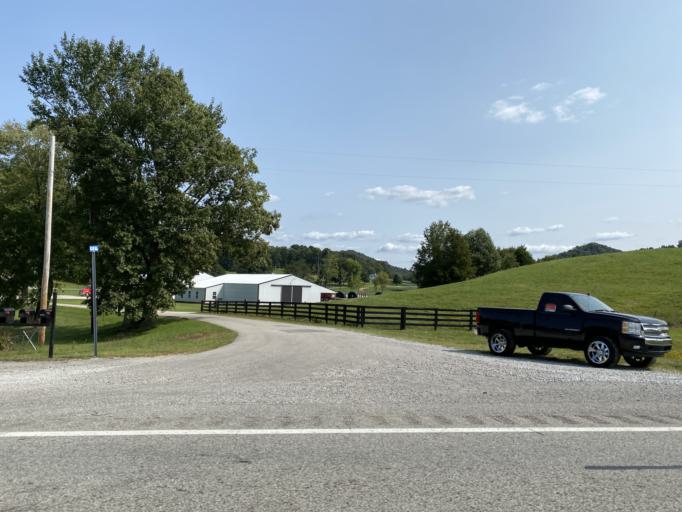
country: US
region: Kentucky
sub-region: Marion County
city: Lebanon
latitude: 37.4882
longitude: -85.2994
